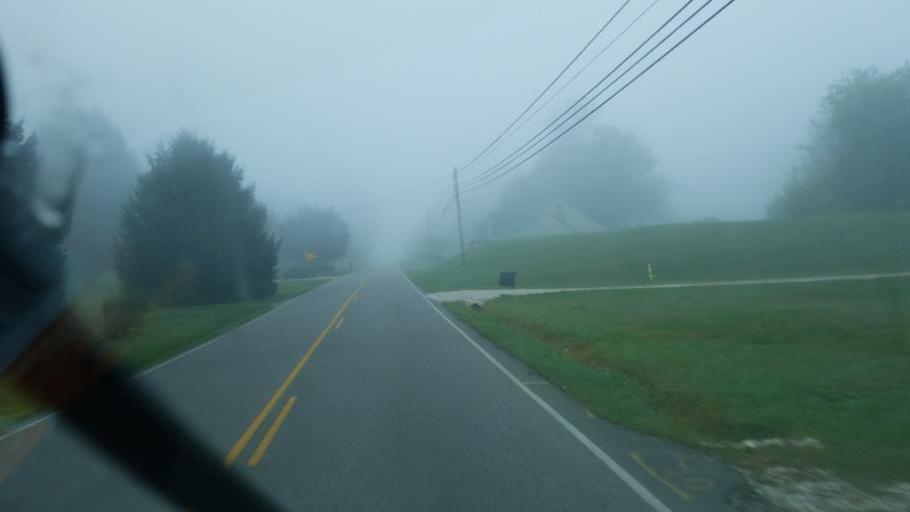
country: US
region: Ohio
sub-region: Scioto County
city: Portsmouth
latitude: 38.7163
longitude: -83.0220
